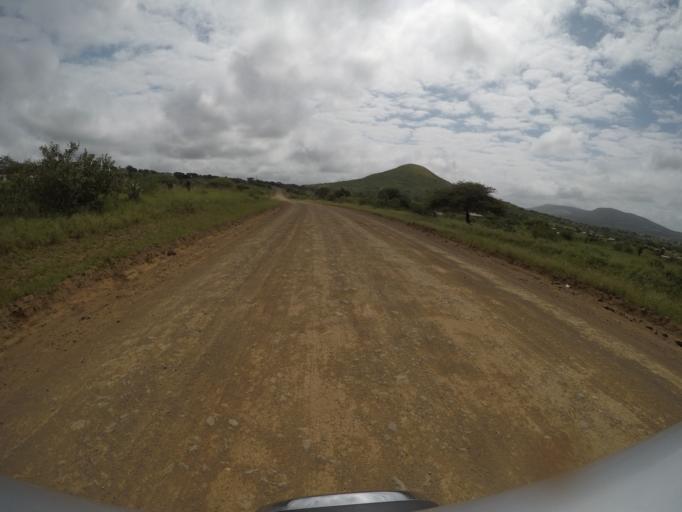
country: ZA
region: KwaZulu-Natal
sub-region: uThungulu District Municipality
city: Empangeni
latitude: -28.6075
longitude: 31.8478
